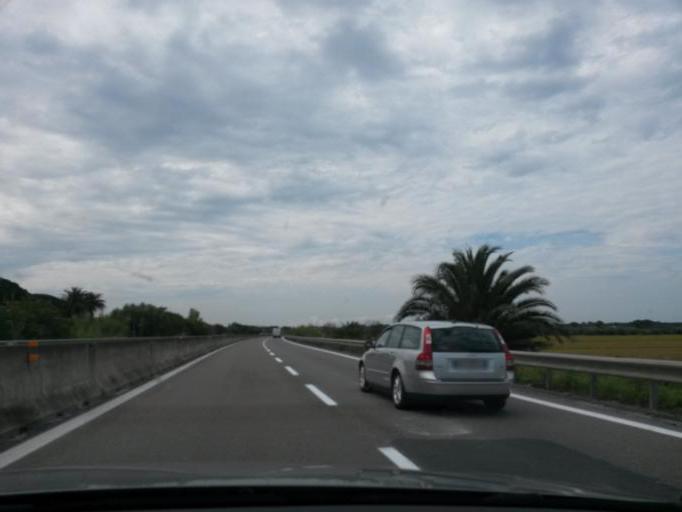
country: IT
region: Tuscany
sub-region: Provincia di Livorno
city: Donoratico
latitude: 43.1672
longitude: 10.5626
